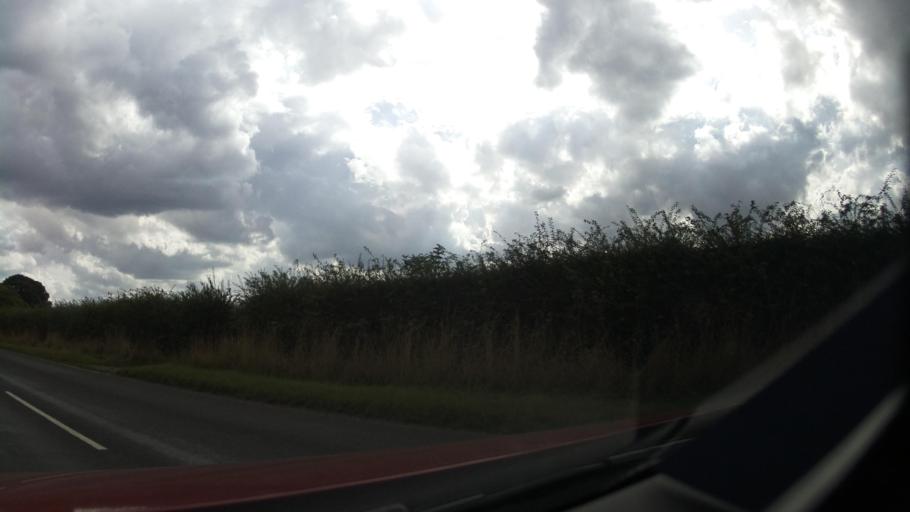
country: GB
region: England
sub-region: North Yorkshire
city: Ripon
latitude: 54.1667
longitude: -1.5499
